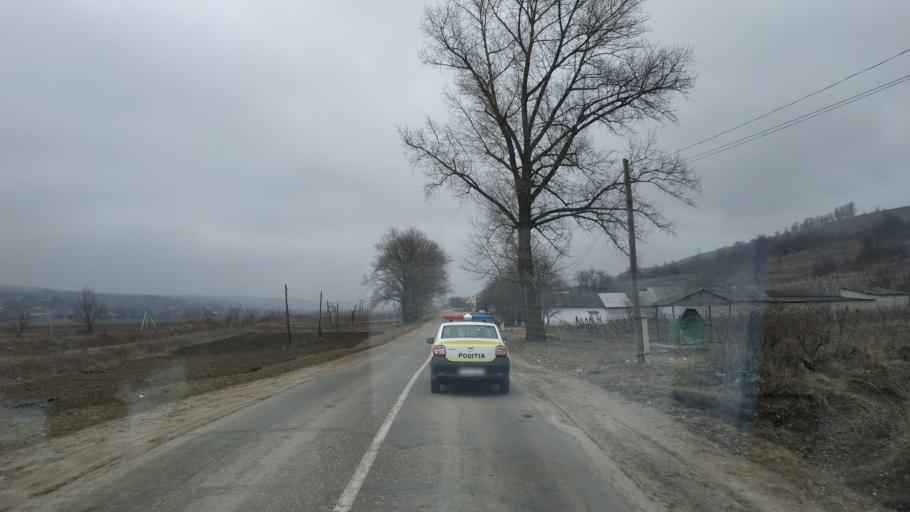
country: MD
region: Hincesti
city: Hincesti
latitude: 46.9739
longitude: 28.4720
